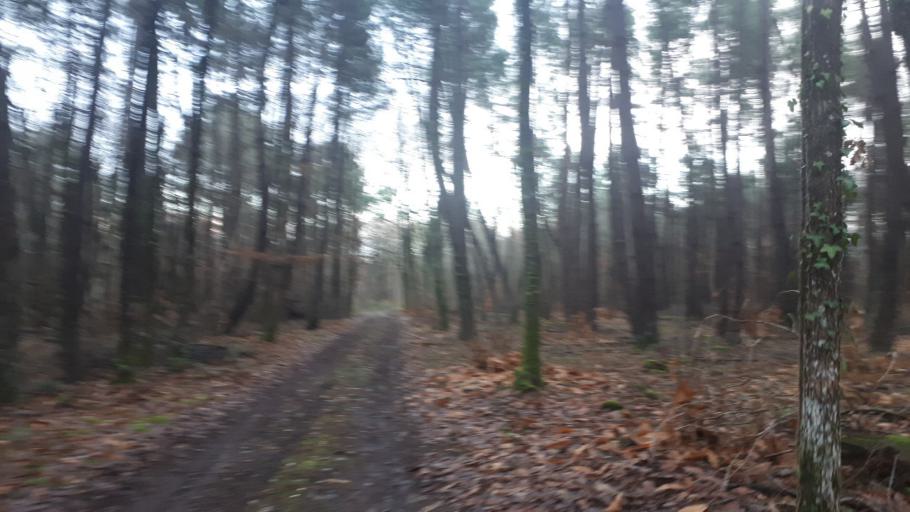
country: FR
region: Centre
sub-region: Departement du Loir-et-Cher
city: Saint-Romain-sur-Cher
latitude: 47.3427
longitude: 1.3945
